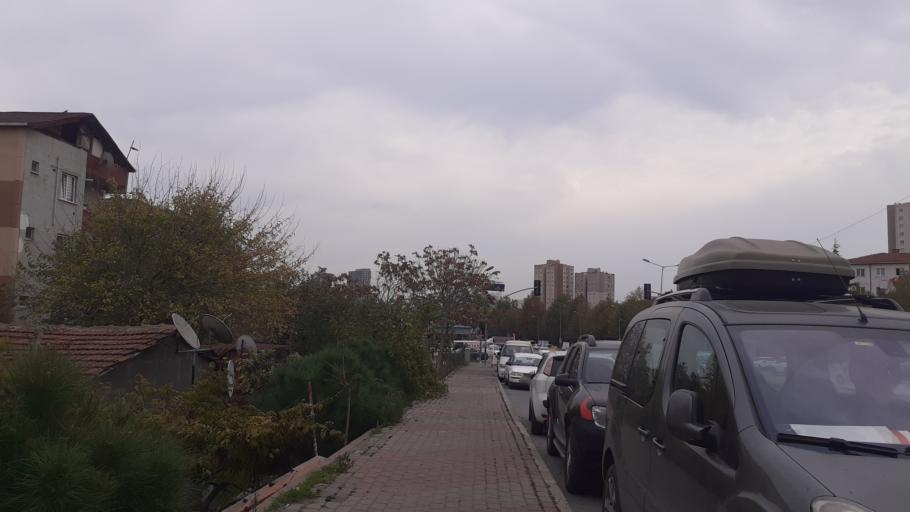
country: TR
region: Istanbul
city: Mahmutbey
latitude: 41.0494
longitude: 28.7973
